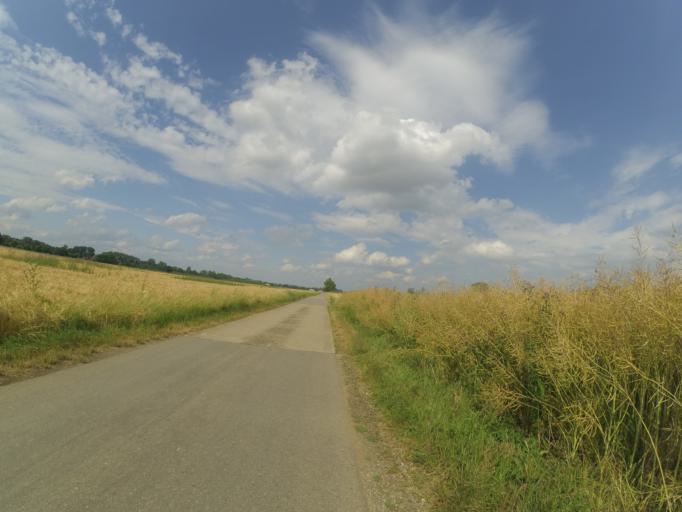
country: DE
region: Baden-Wuerttemberg
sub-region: Tuebingen Region
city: Opfingen
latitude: 48.2815
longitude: 9.8200
